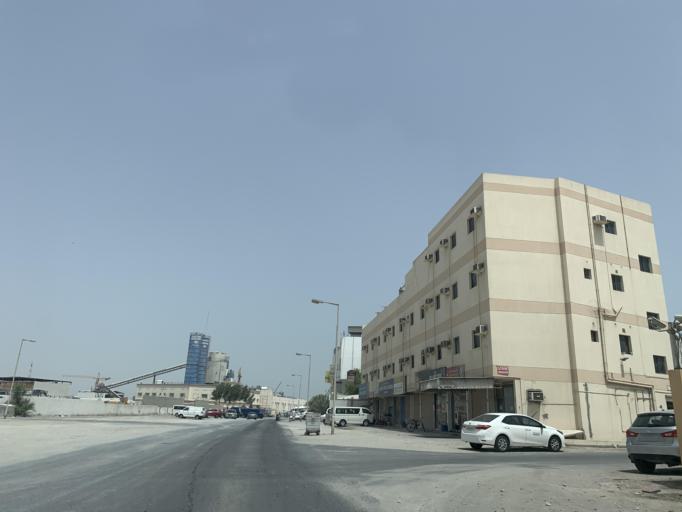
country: BH
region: Northern
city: Sitrah
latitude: 26.1455
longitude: 50.5998
